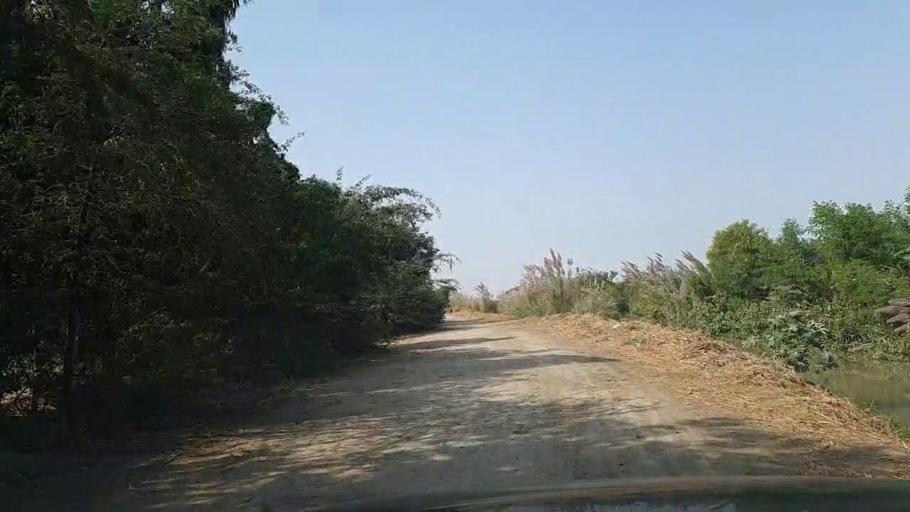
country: PK
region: Sindh
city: Gharo
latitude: 24.7032
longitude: 67.6433
